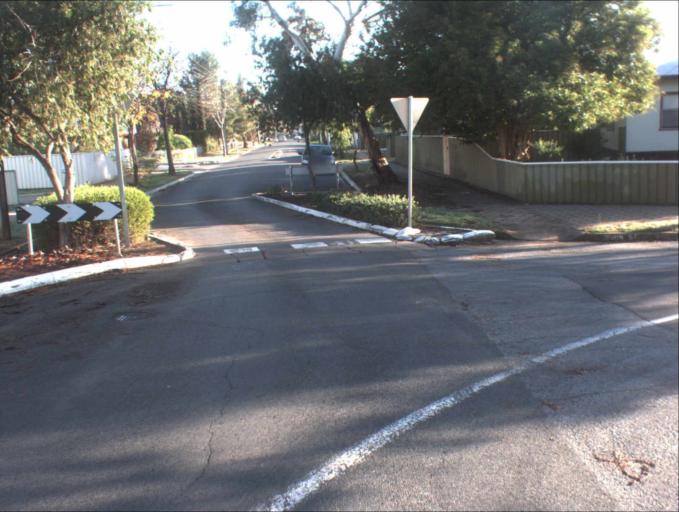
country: AU
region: South Australia
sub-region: Port Adelaide Enfield
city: Gilles Plains
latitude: -34.8677
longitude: 138.6514
